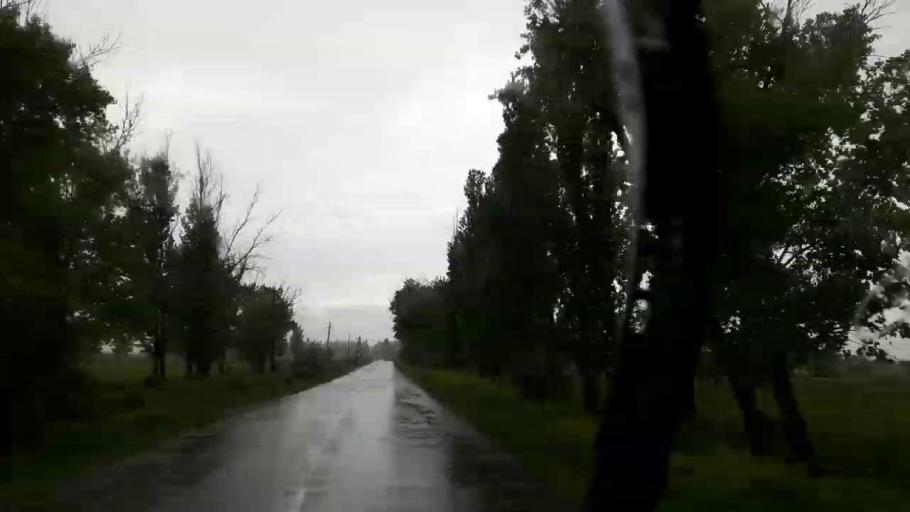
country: GE
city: Agara
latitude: 42.0124
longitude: 43.7898
